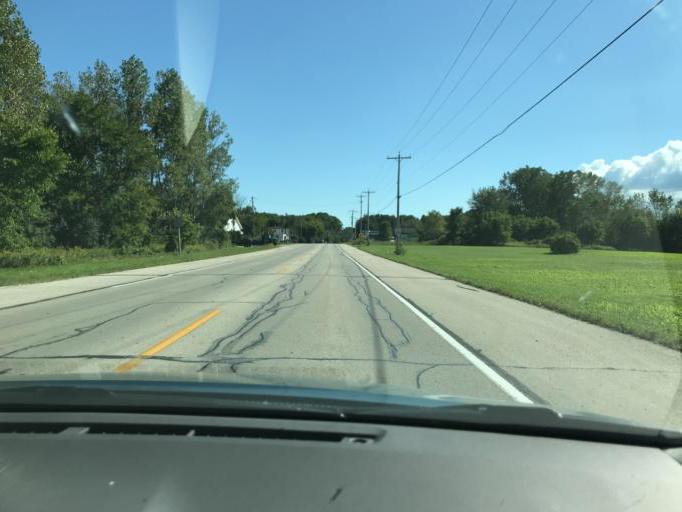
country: US
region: Illinois
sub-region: Lake County
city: Winthrop Harbor
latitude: 42.4957
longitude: -87.8221
